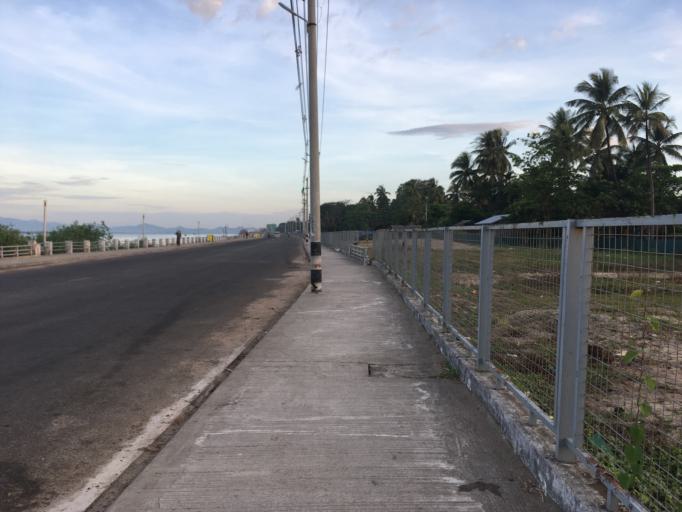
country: MM
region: Mon
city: Mawlamyine
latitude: 16.4573
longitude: 97.6236
